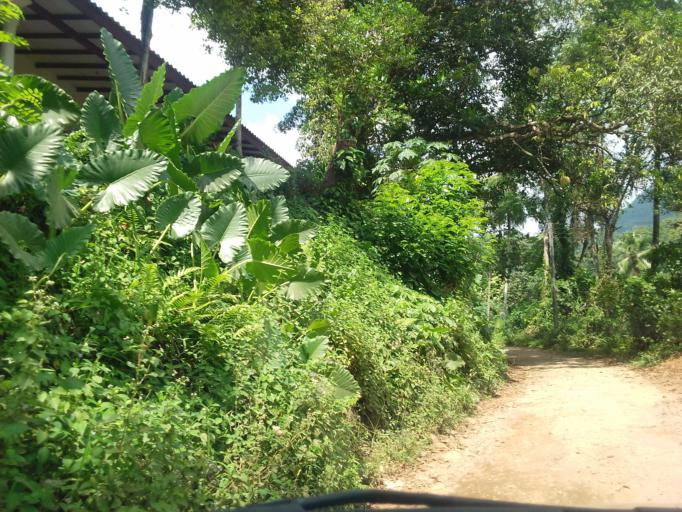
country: LK
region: Central
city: Gampola
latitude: 7.0136
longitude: 80.3551
